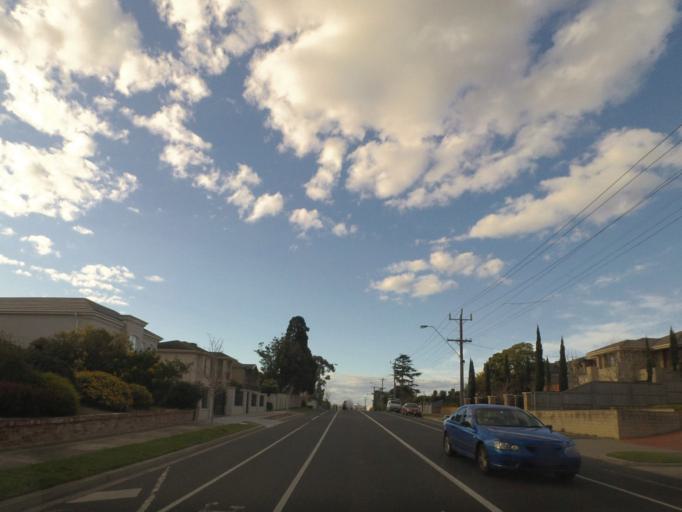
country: AU
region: Victoria
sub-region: Boroondara
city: Balwyn North
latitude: -37.8055
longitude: 145.0827
